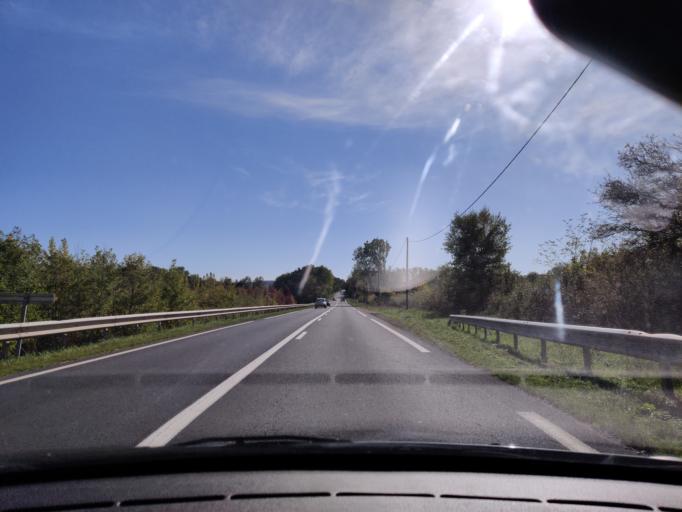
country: FR
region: Auvergne
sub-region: Departement du Puy-de-Dome
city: Combronde
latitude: 46.0108
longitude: 3.0908
